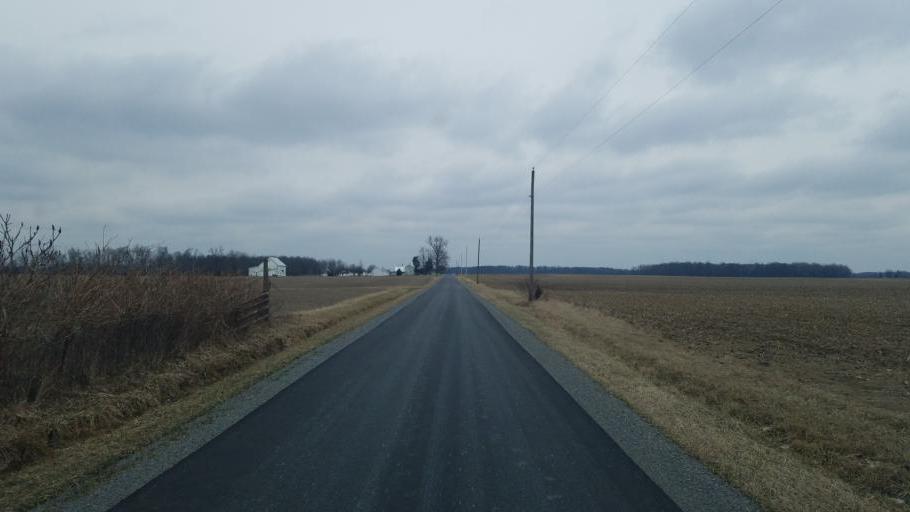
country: US
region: Ohio
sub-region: Morrow County
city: Mount Gilead
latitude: 40.5868
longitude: -82.8950
